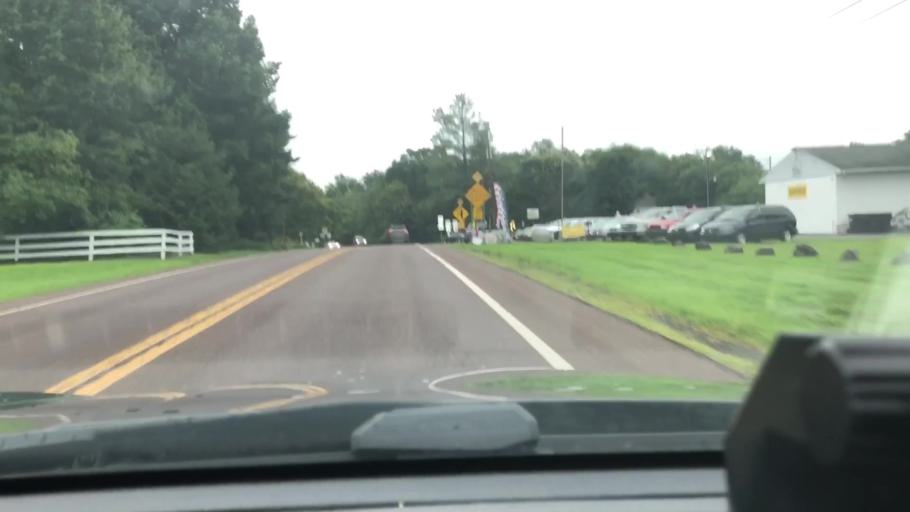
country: US
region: Pennsylvania
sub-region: Montgomery County
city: Gilbertsville
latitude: 40.3173
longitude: -75.5715
